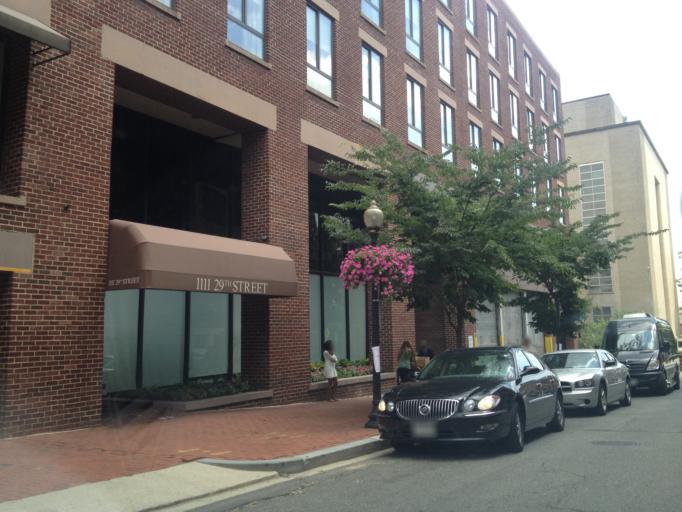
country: US
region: Washington, D.C.
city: Washington, D.C.
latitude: 38.9047
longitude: -77.0581
